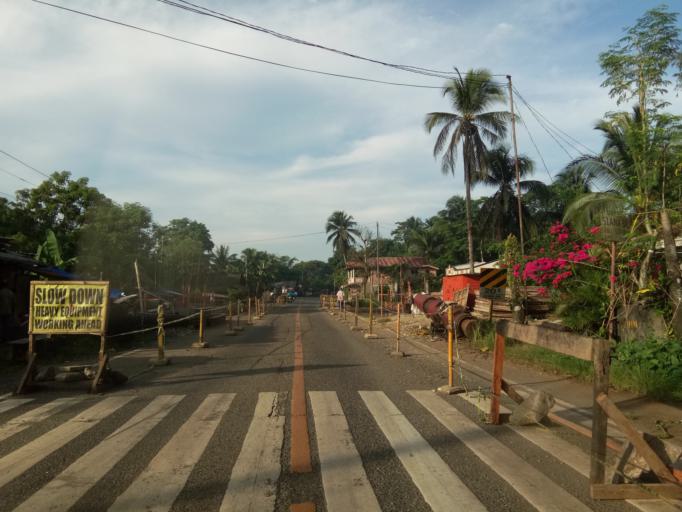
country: PH
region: Caraga
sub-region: Province of Surigao del Norte
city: Tubod
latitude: 9.5423
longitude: 125.5658
